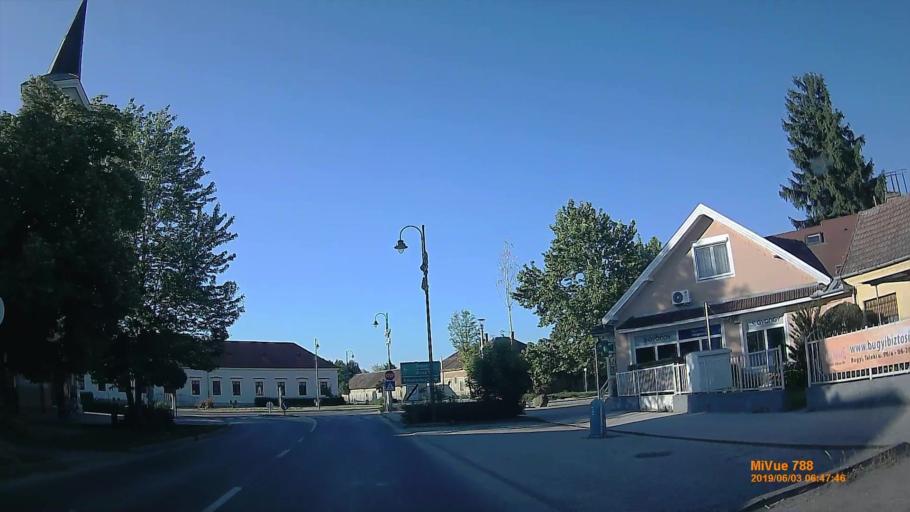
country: HU
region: Pest
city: Bugyi
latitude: 47.2238
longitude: 19.1498
